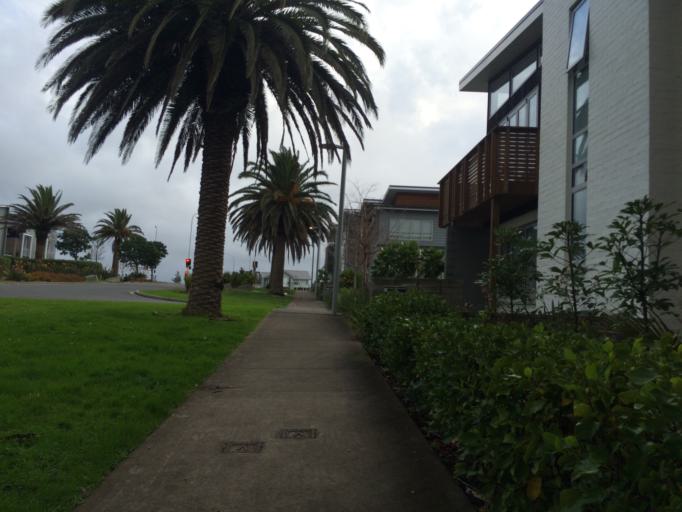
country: NZ
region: Auckland
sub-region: Auckland
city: Rosebank
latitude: -36.7923
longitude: 174.6570
